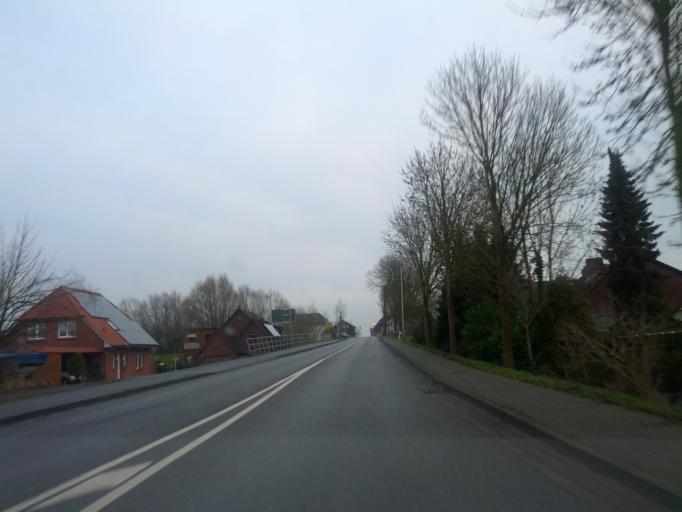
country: DE
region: Lower Saxony
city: Jork
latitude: 53.5199
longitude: 9.7272
